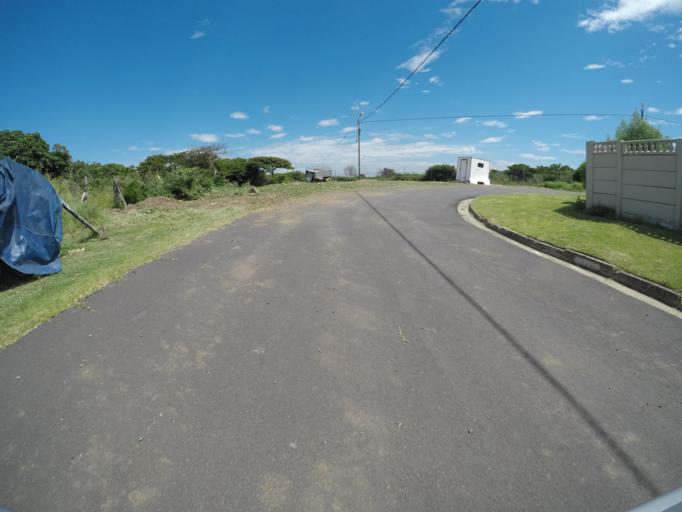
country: ZA
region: Eastern Cape
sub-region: Buffalo City Metropolitan Municipality
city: East London
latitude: -33.0391
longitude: 27.8834
